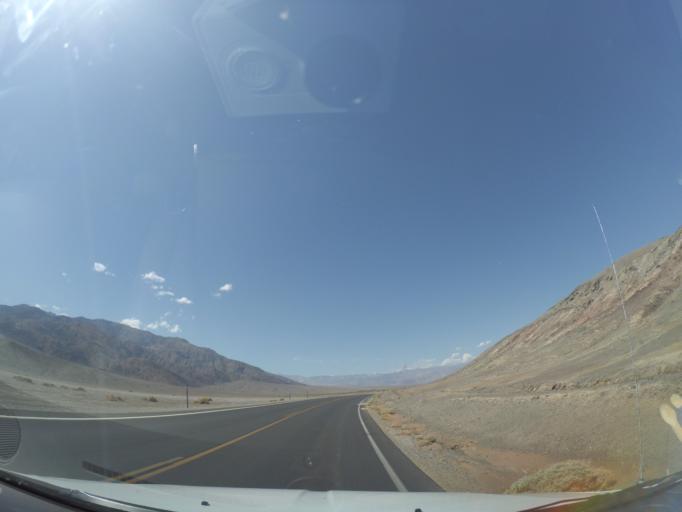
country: US
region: Nevada
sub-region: Nye County
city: Beatty
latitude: 36.6132
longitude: -117.0785
